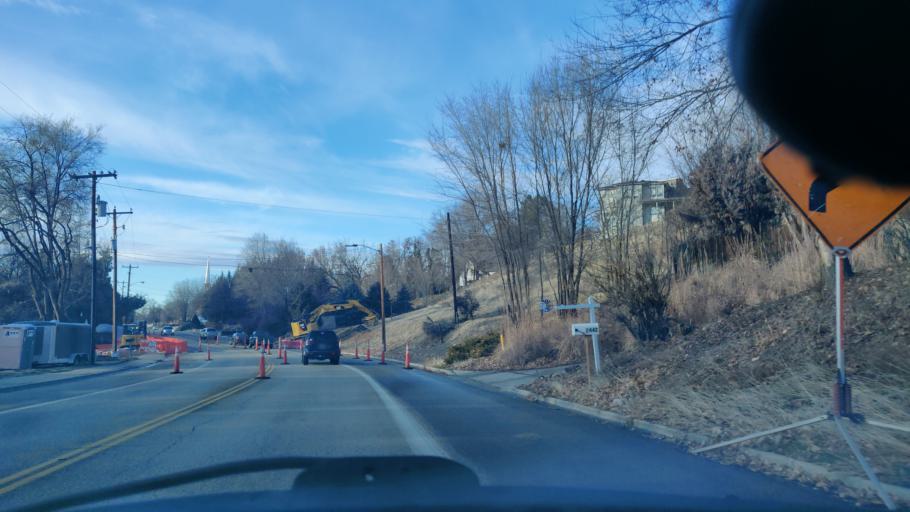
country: US
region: Idaho
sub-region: Ada County
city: Garden City
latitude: 43.6467
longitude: -116.2191
